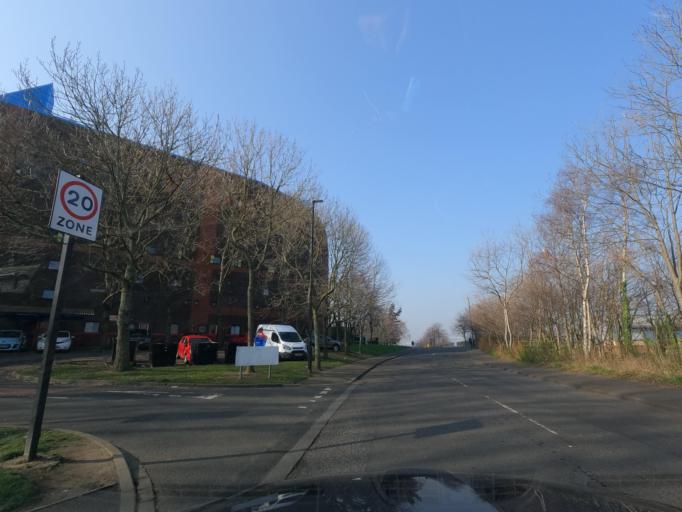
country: GB
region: England
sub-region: Gateshead
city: Felling
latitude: 54.9763
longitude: -1.5757
